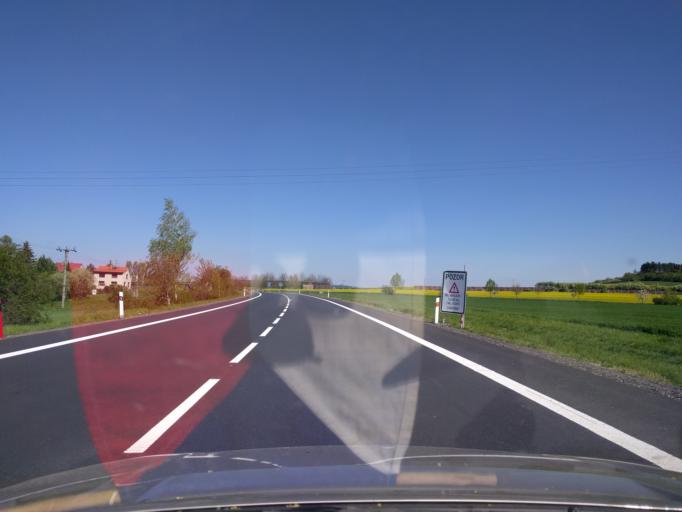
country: CZ
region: Central Bohemia
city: Prerov nad Labem
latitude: 50.1332
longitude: 14.8462
